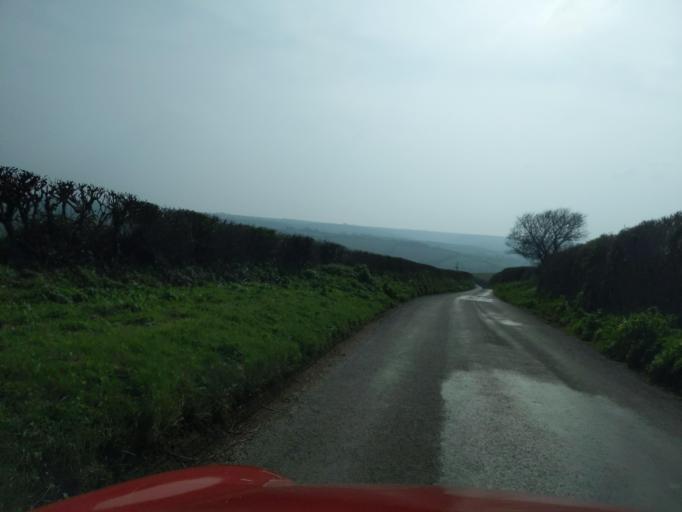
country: GB
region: England
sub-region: Devon
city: Salcombe
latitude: 50.2556
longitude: -3.7143
